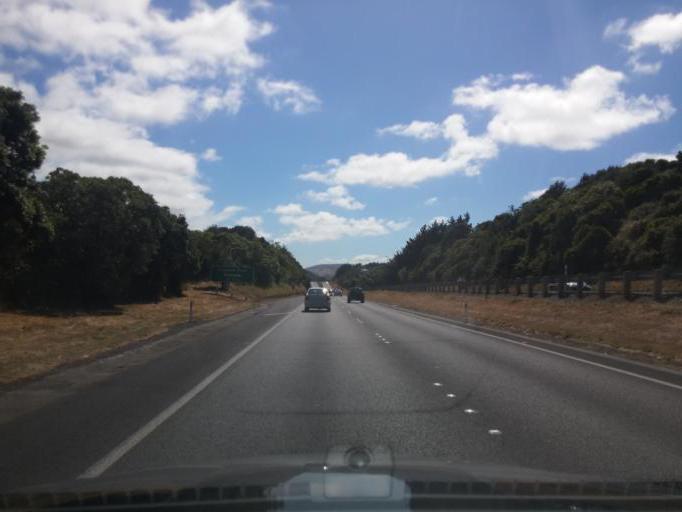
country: NZ
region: Wellington
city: Petone
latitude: -41.2143
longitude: 174.8133
